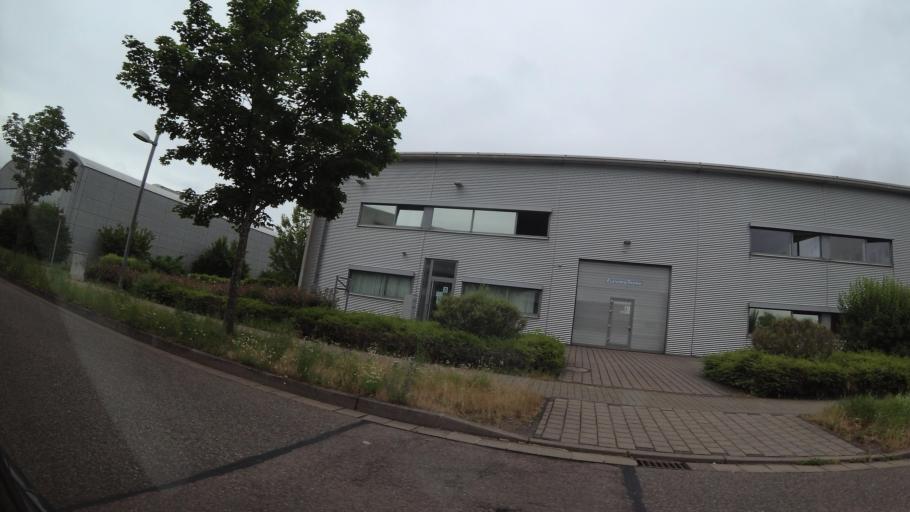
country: DE
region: Saarland
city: Saarbrucken
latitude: 49.2398
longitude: 6.9516
